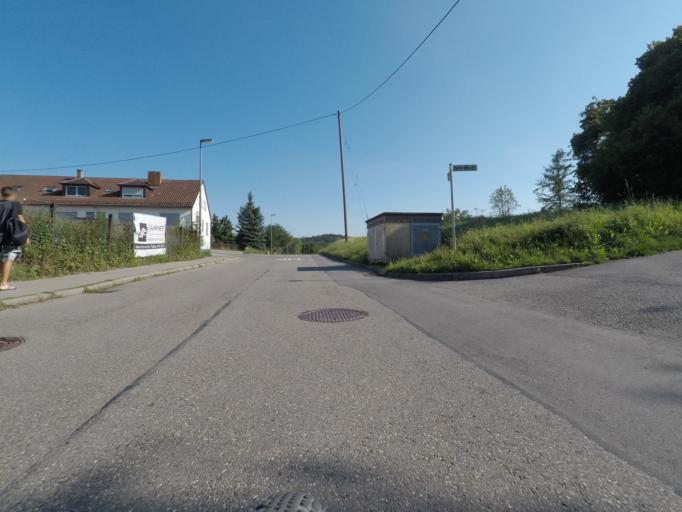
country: DE
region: Baden-Wuerttemberg
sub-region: Regierungsbezirk Stuttgart
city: Hildrizhausen
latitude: 48.6239
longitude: 8.9711
